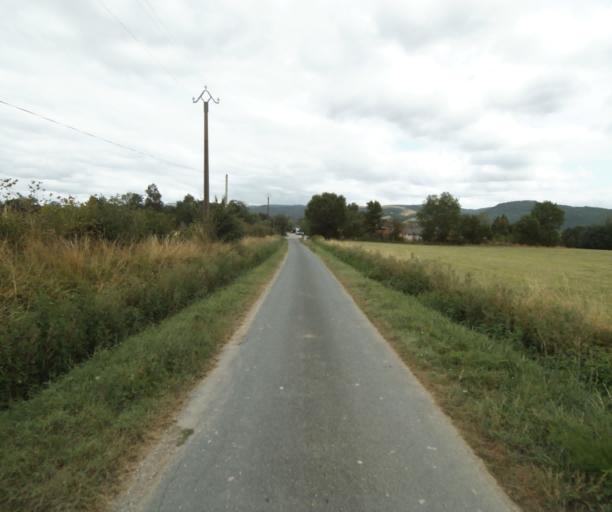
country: FR
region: Midi-Pyrenees
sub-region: Departement du Tarn
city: Soreze
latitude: 43.4705
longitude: 2.0574
